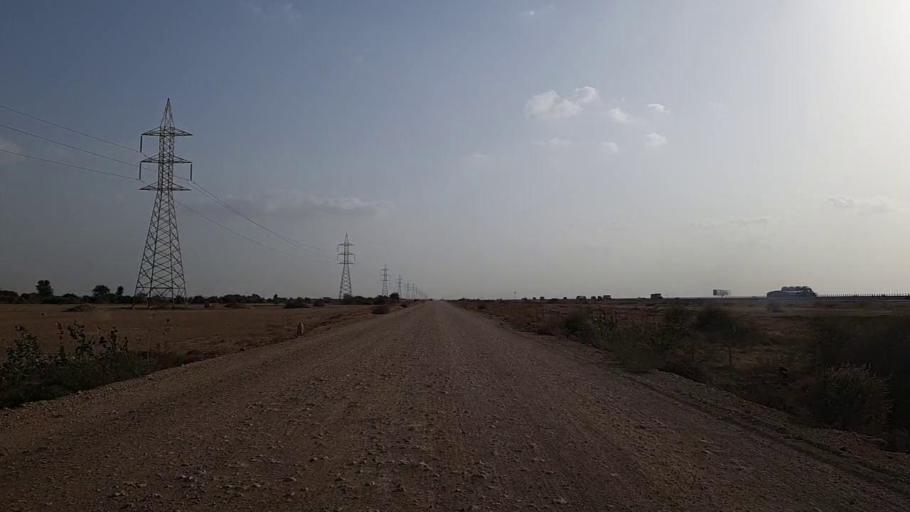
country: PK
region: Sindh
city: Kotri
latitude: 25.2129
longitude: 67.9012
